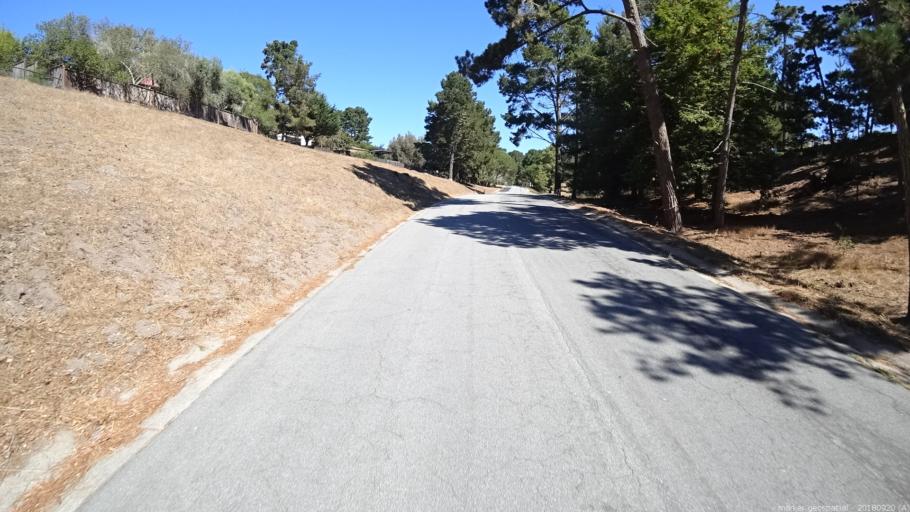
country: US
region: California
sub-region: Monterey County
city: Carmel-by-the-Sea
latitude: 36.5636
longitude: -121.9069
